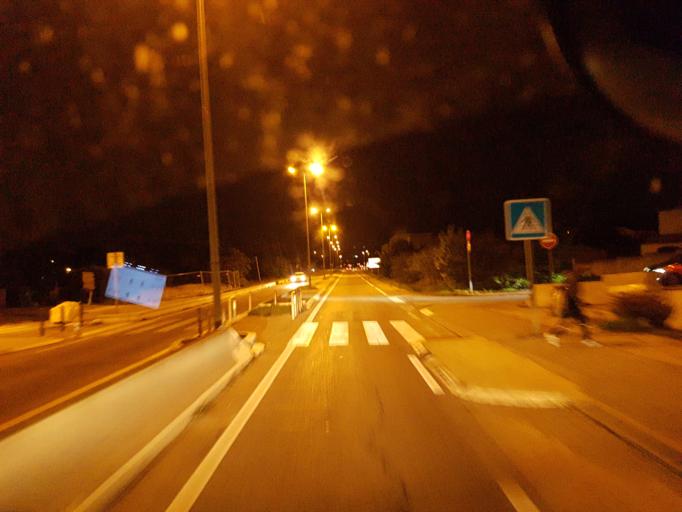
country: FR
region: Provence-Alpes-Cote d'Azur
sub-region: Departement des Bouches-du-Rhone
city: Gignac-la-Nerthe
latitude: 43.3951
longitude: 5.2348
